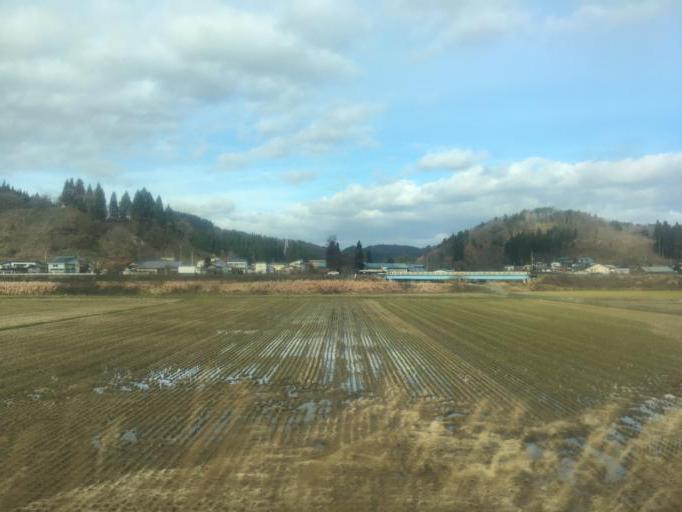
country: JP
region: Akita
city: Takanosu
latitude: 40.2182
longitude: 140.3198
